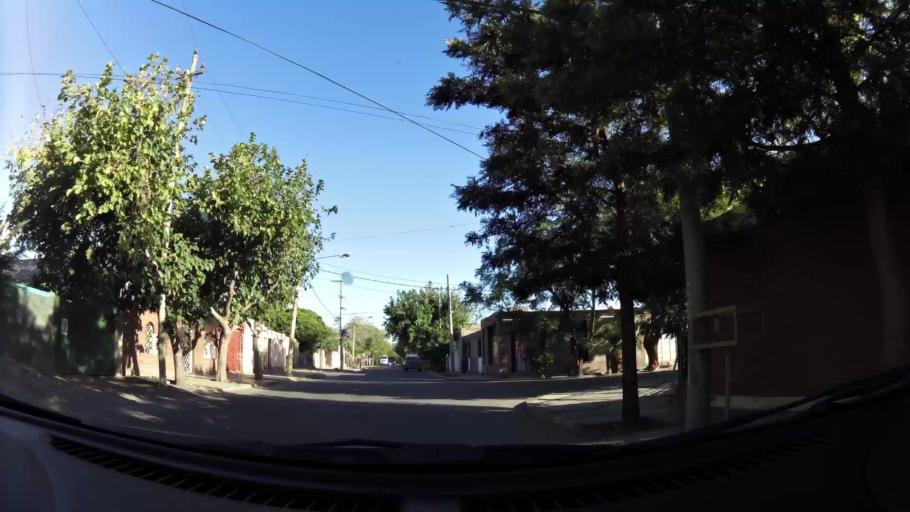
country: AR
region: San Juan
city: San Juan
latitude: -31.5489
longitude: -68.5181
